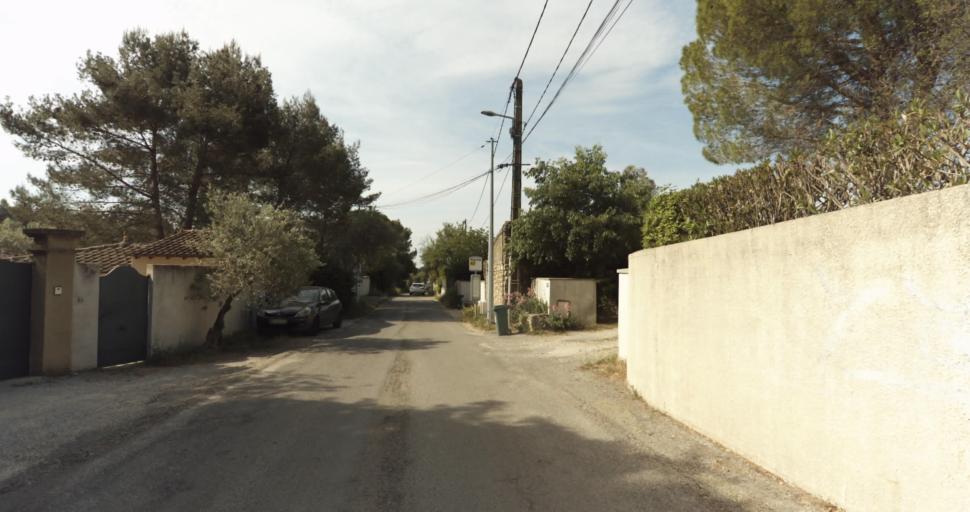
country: FR
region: Languedoc-Roussillon
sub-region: Departement du Gard
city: Nimes
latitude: 43.8617
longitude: 4.3834
